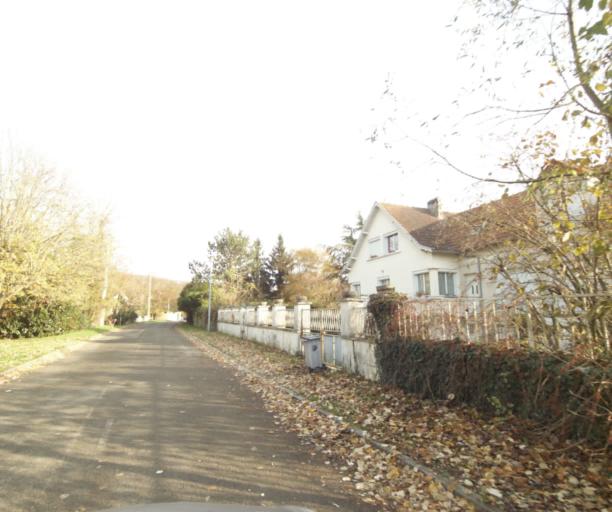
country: FR
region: Ile-de-France
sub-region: Departement des Yvelines
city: Conflans-Sainte-Honorine
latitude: 48.9892
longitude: 2.0888
